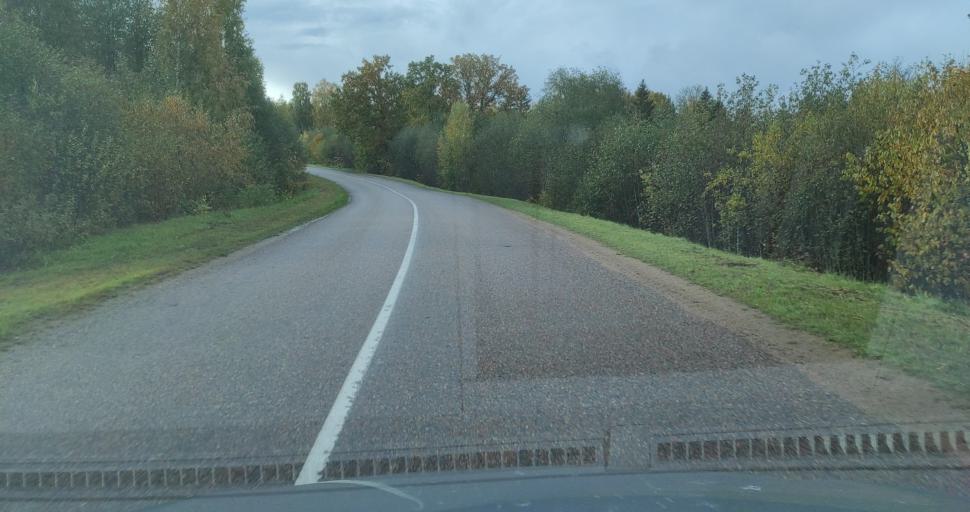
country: LV
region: Skrunda
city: Skrunda
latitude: 56.5981
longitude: 21.9038
